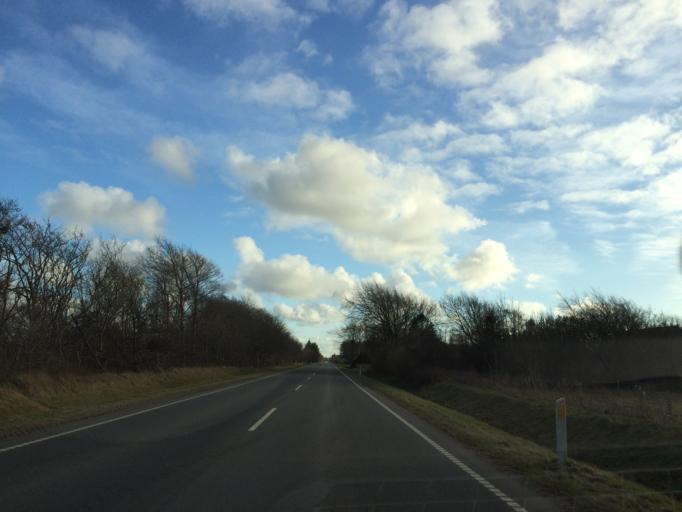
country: DK
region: Central Jutland
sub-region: Holstebro Kommune
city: Ulfborg
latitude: 56.3522
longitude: 8.3391
